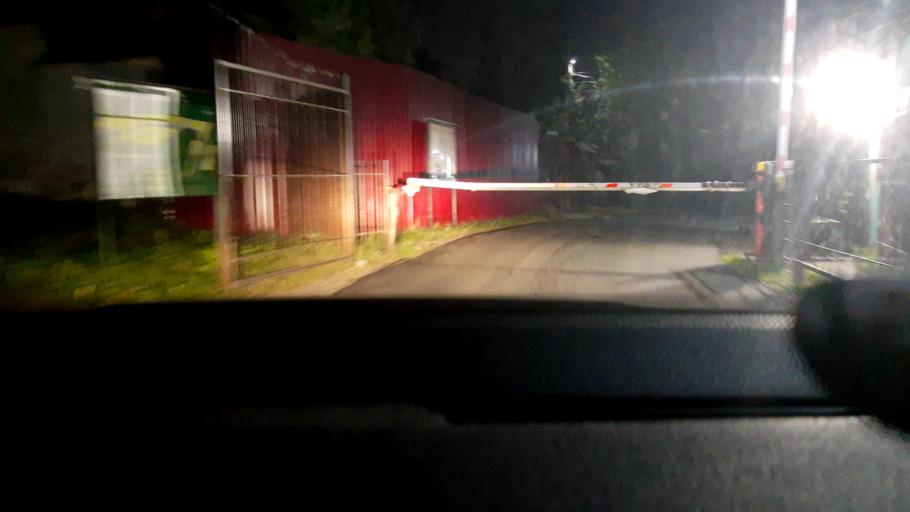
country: RU
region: Moskovskaya
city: Skhodnya
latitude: 55.8918
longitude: 37.2825
